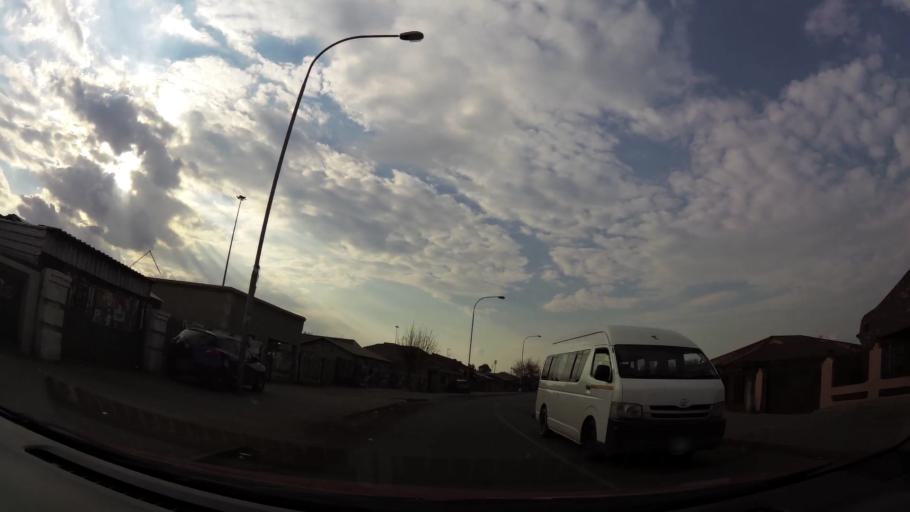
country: ZA
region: Gauteng
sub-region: Sedibeng District Municipality
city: Vanderbijlpark
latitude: -26.6954
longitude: 27.8657
